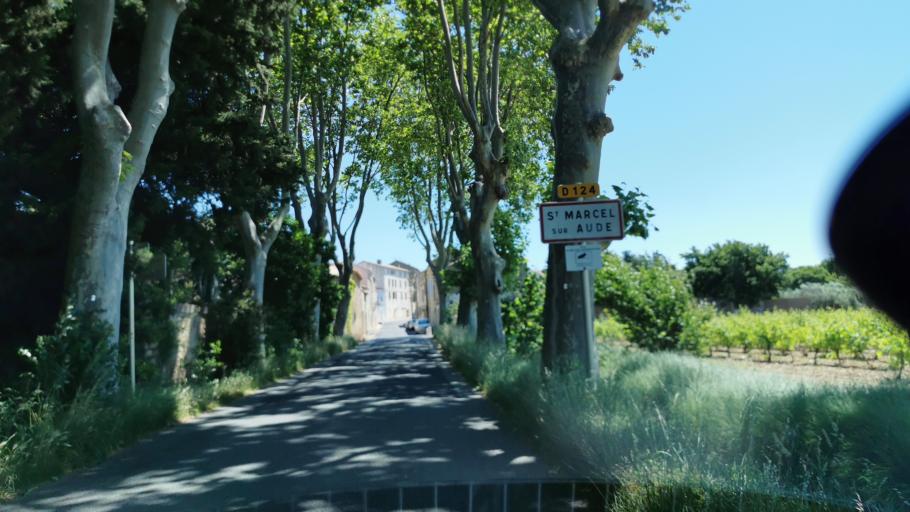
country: FR
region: Languedoc-Roussillon
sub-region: Departement de l'Aude
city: Saint-Marcel-sur-Aude
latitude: 43.2431
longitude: 2.9198
